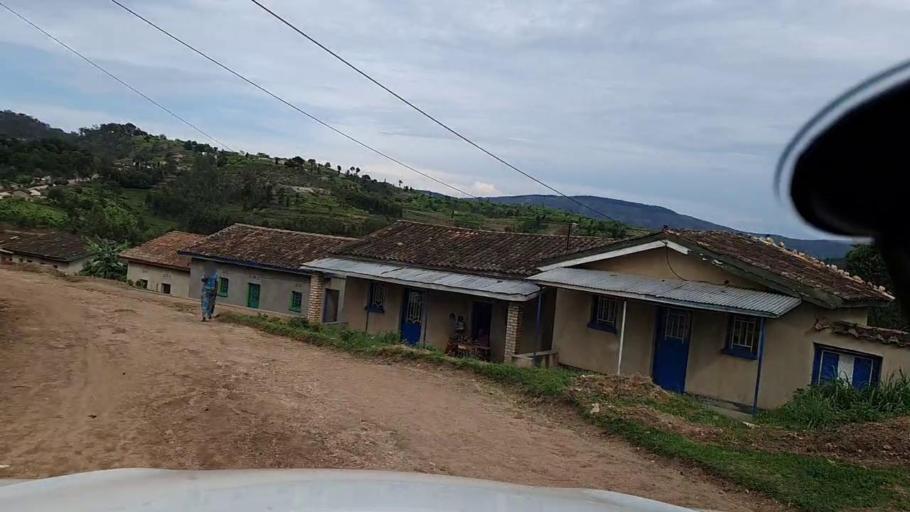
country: RW
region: Southern Province
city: Gitarama
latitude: -2.1295
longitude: 29.6568
